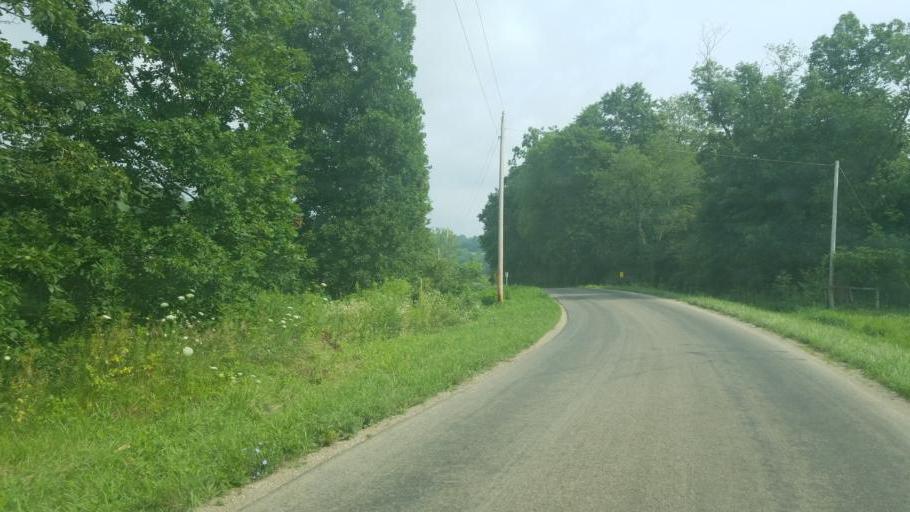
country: US
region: Ohio
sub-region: Sandusky County
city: Bellville
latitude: 40.5489
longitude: -82.3779
